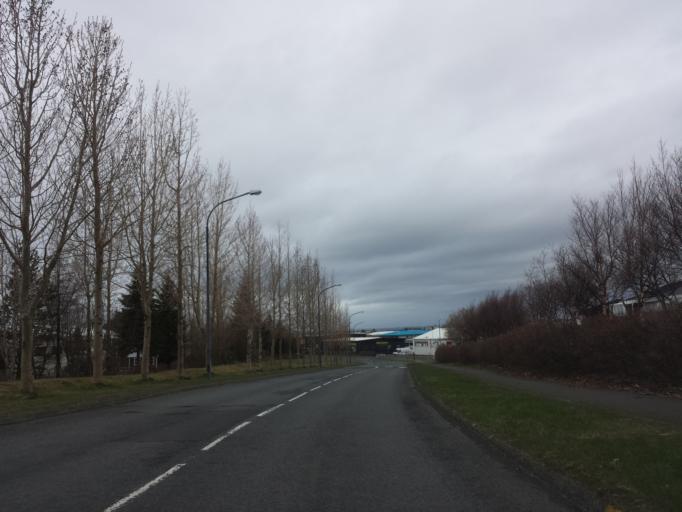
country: IS
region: Capital Region
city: Gardabaer
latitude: 64.0905
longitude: -21.8956
